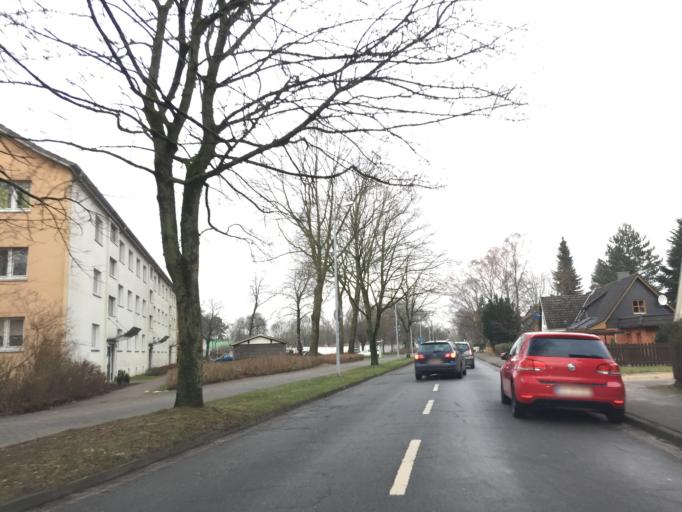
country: DE
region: Schleswig-Holstein
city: Wahlstedt
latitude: 53.9508
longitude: 10.2013
